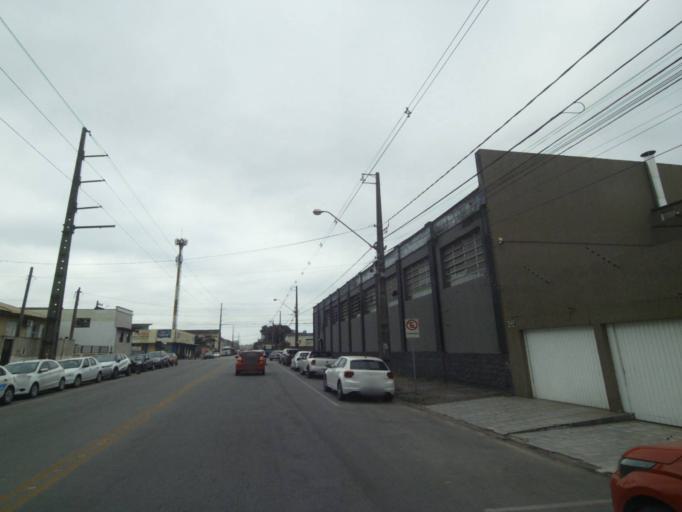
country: BR
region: Parana
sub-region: Paranagua
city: Paranagua
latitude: -25.5138
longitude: -48.5155
